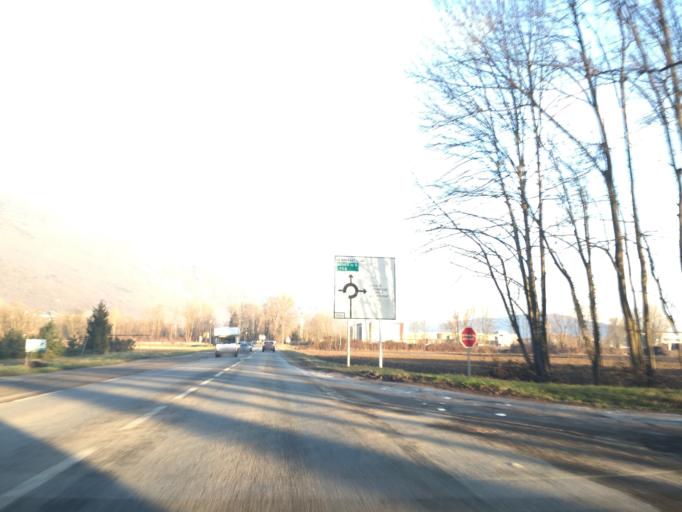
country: FR
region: Rhone-Alpes
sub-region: Departement de la Savoie
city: Le Bourget-du-Lac
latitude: 45.6350
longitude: 5.8725
